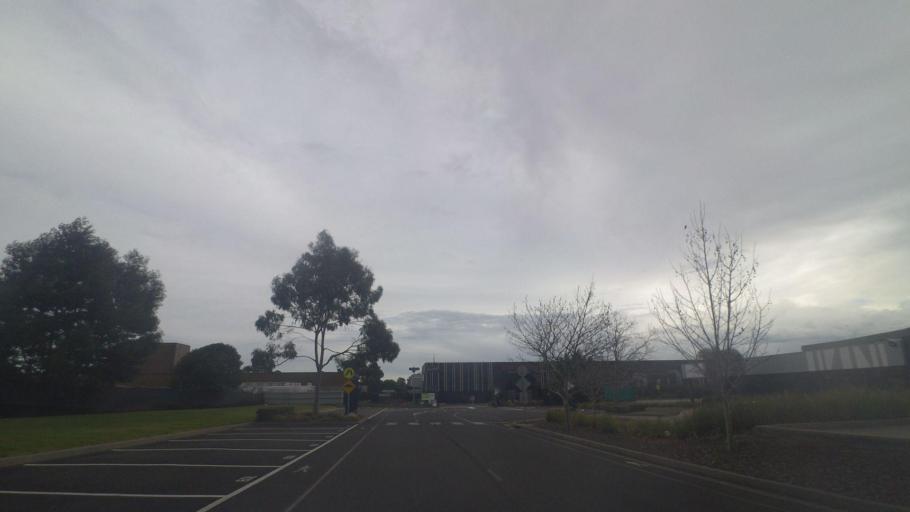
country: AU
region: Victoria
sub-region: Monash
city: Notting Hill
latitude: -37.9034
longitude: 145.1353
